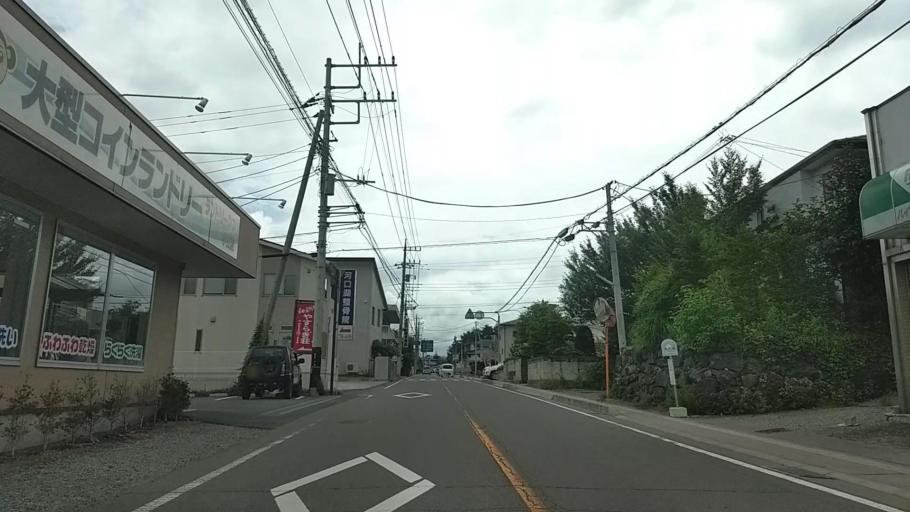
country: JP
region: Yamanashi
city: Fujikawaguchiko
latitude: 35.5048
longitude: 138.7547
